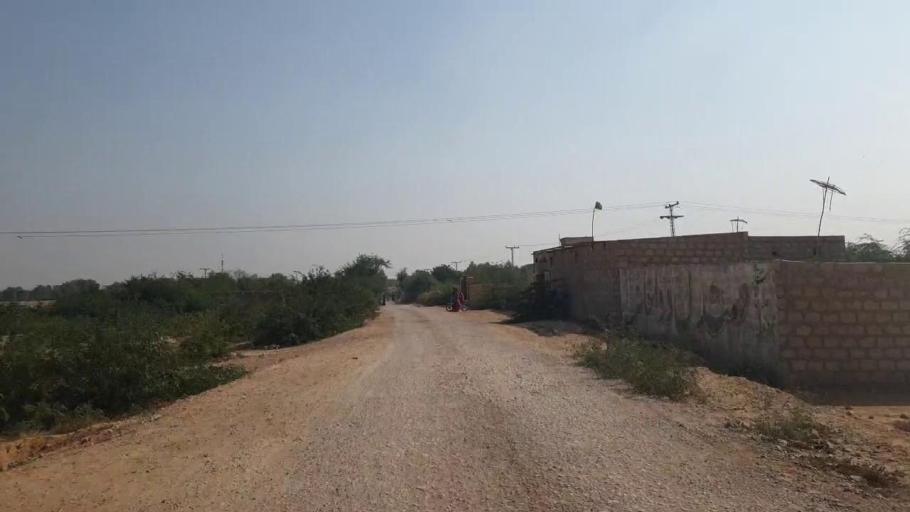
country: PK
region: Sindh
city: Kotri
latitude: 25.3224
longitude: 68.2364
